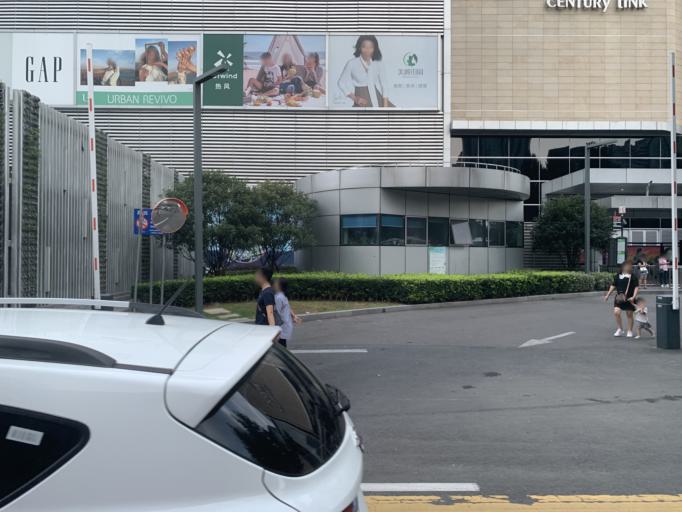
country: CN
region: Shanghai Shi
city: Pudong
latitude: 31.2304
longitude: 121.5215
